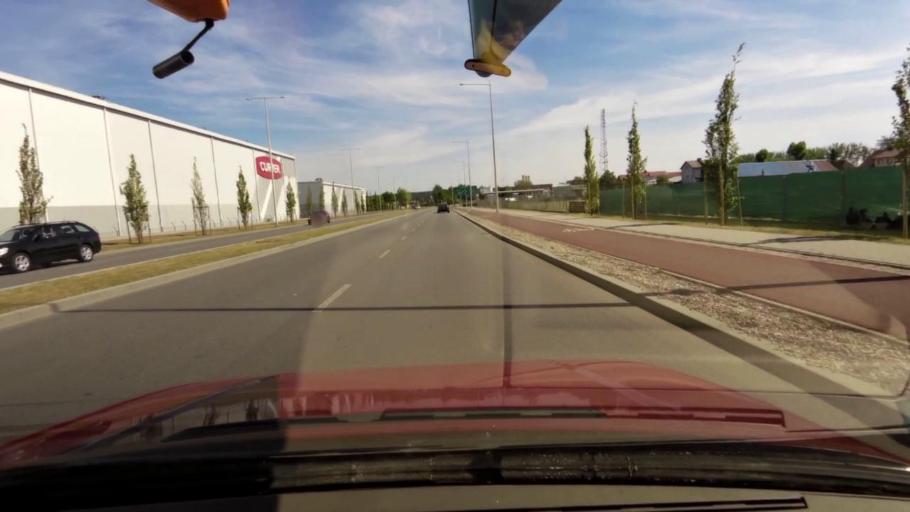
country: PL
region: Pomeranian Voivodeship
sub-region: Slupsk
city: Slupsk
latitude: 54.4539
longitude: 17.0148
